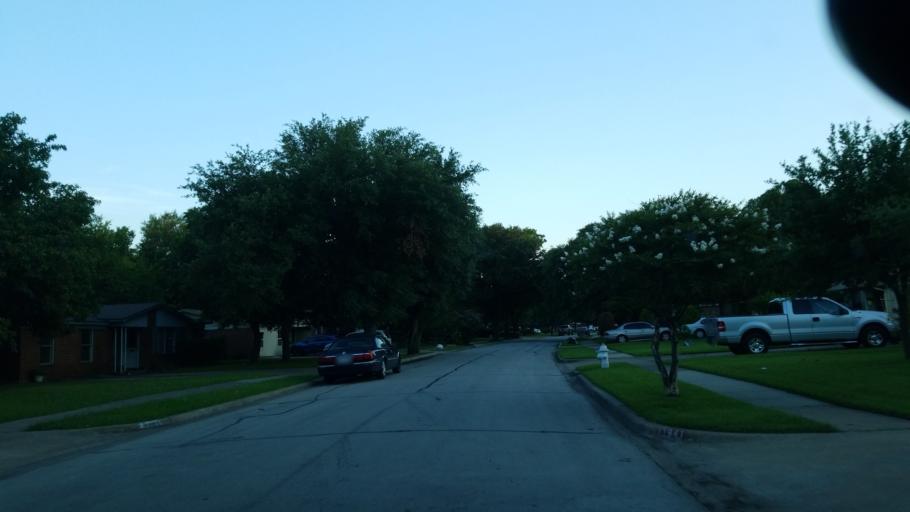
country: US
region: Texas
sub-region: Dallas County
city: Farmers Branch
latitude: 32.9357
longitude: -96.8824
